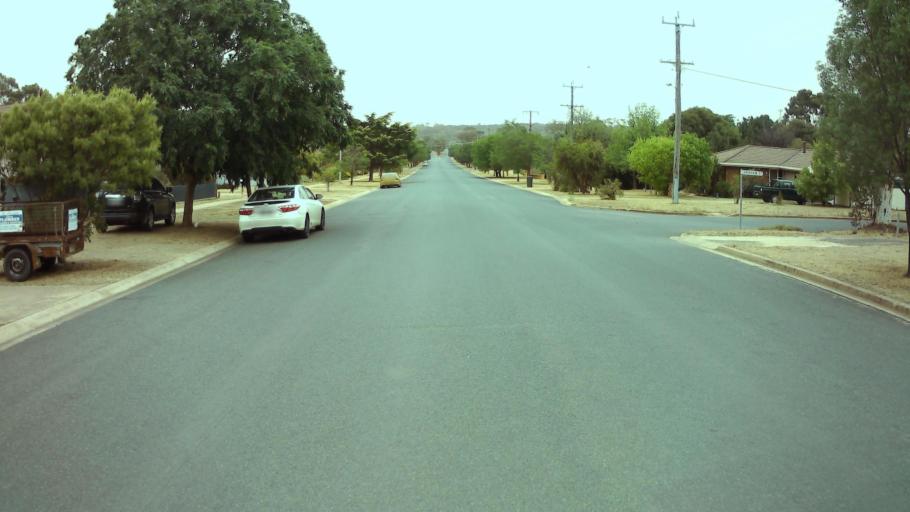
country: AU
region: New South Wales
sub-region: Weddin
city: Grenfell
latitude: -33.9000
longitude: 148.1648
